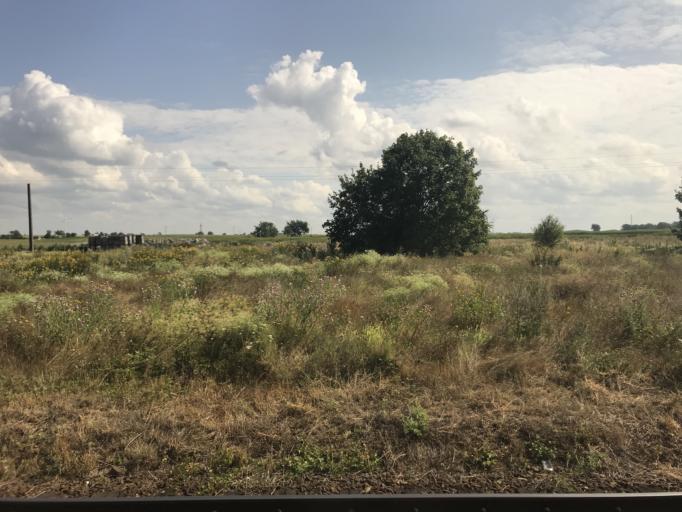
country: PL
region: Kujawsko-Pomorskie
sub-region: Powiat inowroclawski
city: Zlotniki Kujawskie
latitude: 52.9073
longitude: 18.1435
